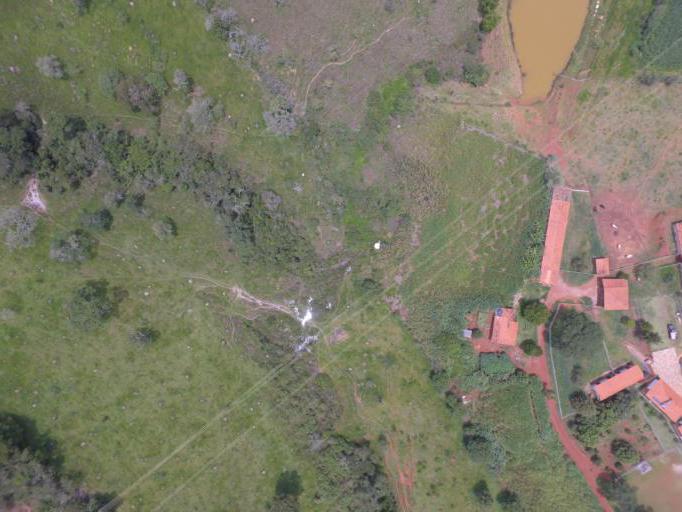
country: BR
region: Minas Gerais
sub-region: Tiradentes
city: Tiradentes
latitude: -21.0449
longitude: -44.0877
